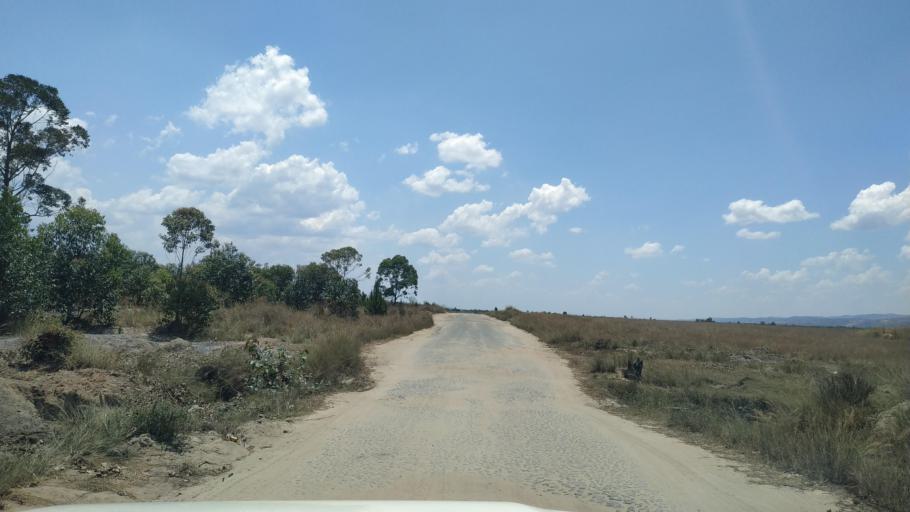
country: MG
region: Analamanga
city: Anjozorobe
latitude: -18.3500
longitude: 48.2668
